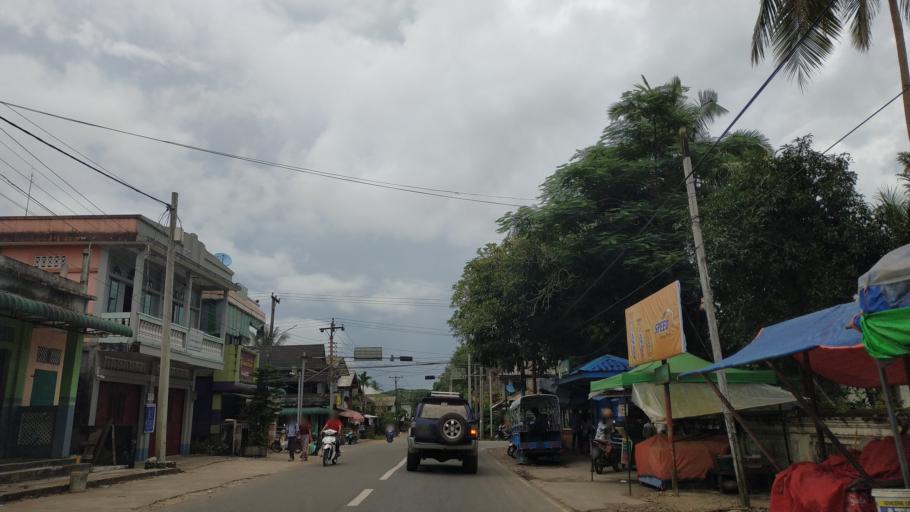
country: MM
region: Tanintharyi
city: Dawei
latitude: 14.0765
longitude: 98.1974
